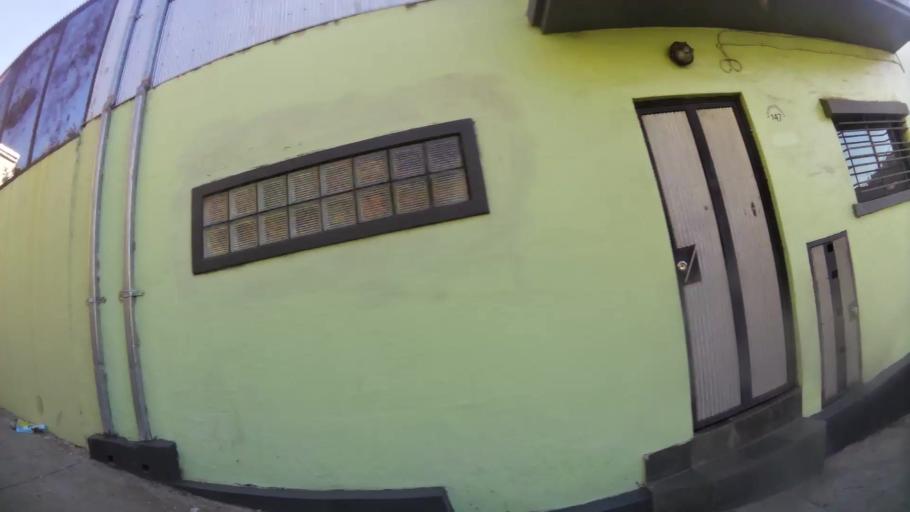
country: CL
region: Valparaiso
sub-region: Provincia de Valparaiso
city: Valparaiso
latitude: -33.0496
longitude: -71.6279
